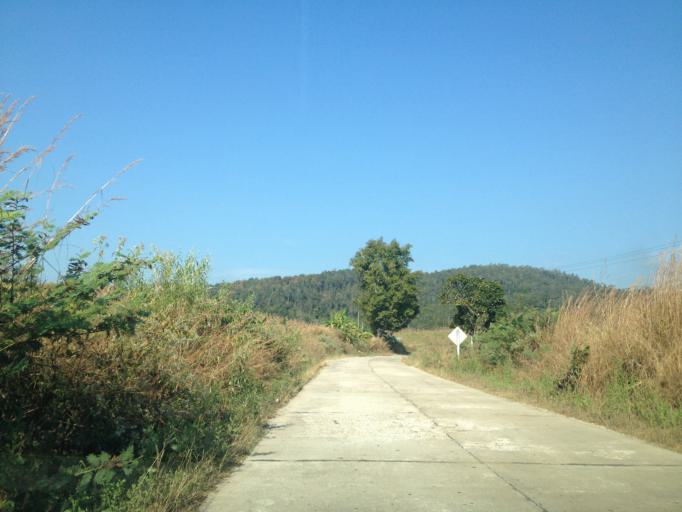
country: TH
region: Mae Hong Son
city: Ban Huai I Huak
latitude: 18.1509
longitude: 98.2165
